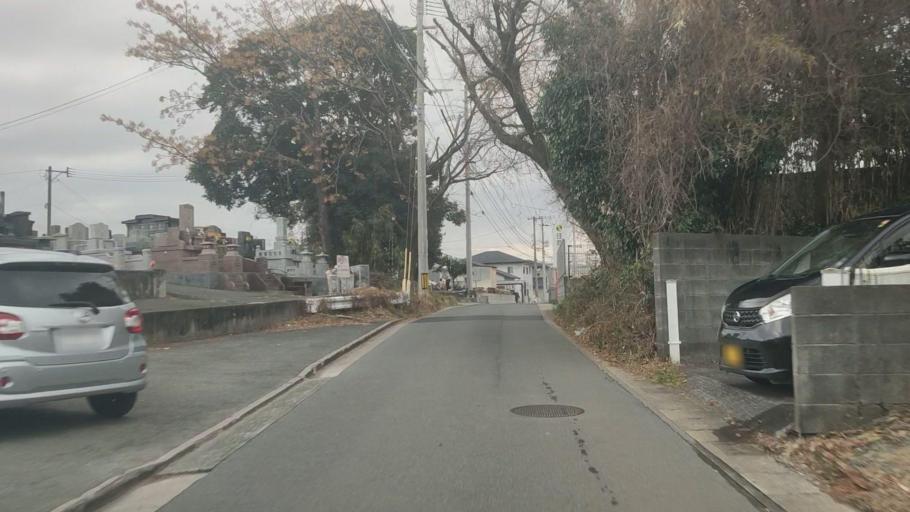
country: JP
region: Kumamoto
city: Ozu
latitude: 32.8296
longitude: 130.7994
